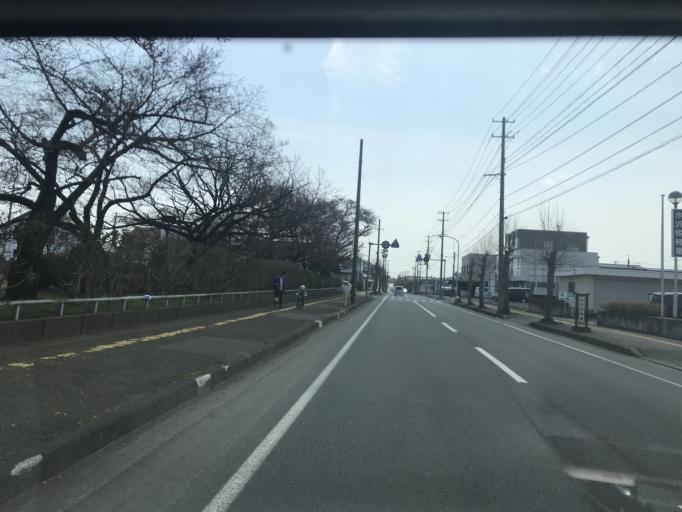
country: JP
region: Iwate
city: Mizusawa
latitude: 39.1342
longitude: 141.1370
